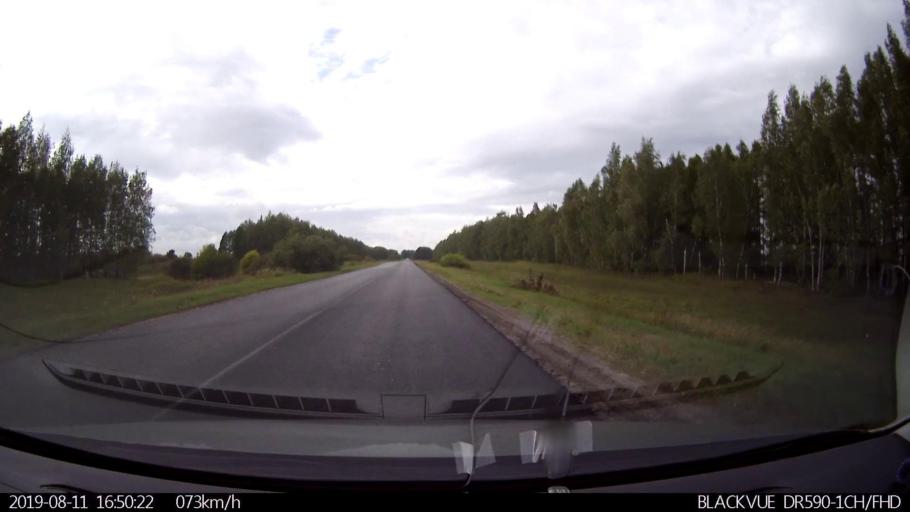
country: RU
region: Ulyanovsk
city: Mayna
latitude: 54.2282
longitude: 47.6882
